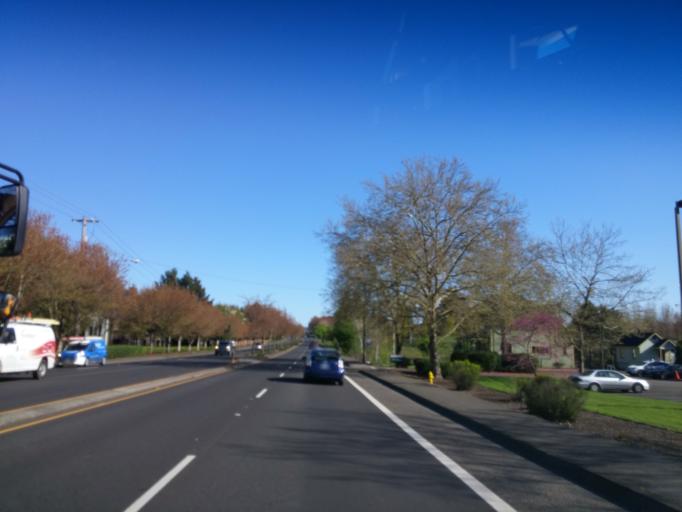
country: US
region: Oregon
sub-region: Washington County
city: Oak Hills
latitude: 45.5204
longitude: -122.8395
